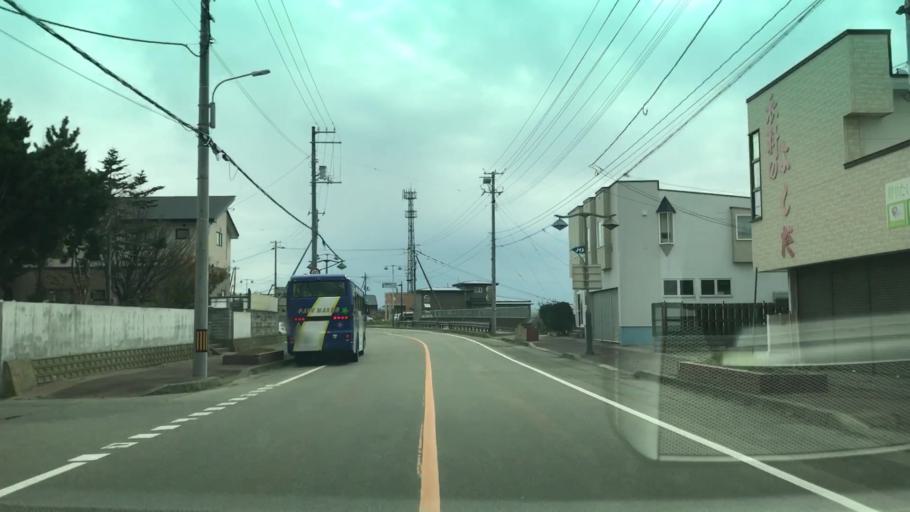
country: JP
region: Hokkaido
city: Shizunai-furukawacho
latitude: 42.0133
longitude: 143.1485
